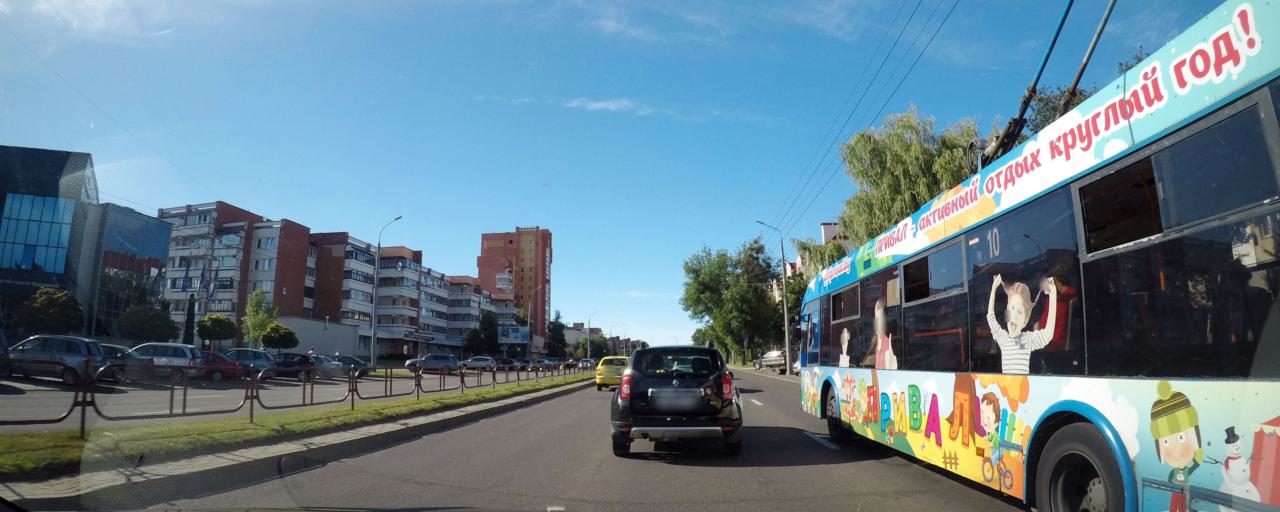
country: BY
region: Grodnenskaya
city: Hrodna
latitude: 53.6949
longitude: 23.8221
